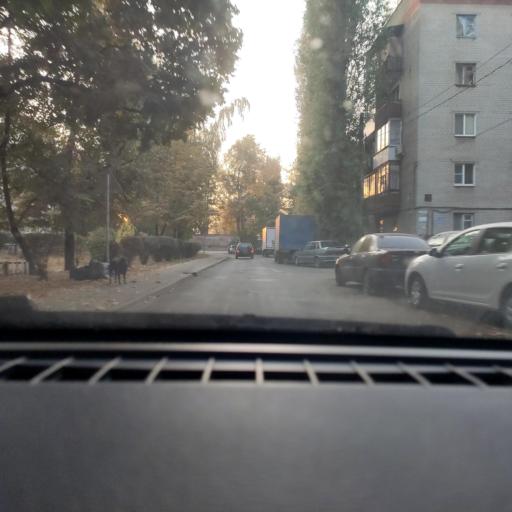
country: RU
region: Voronezj
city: Maslovka
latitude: 51.6133
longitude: 39.2532
